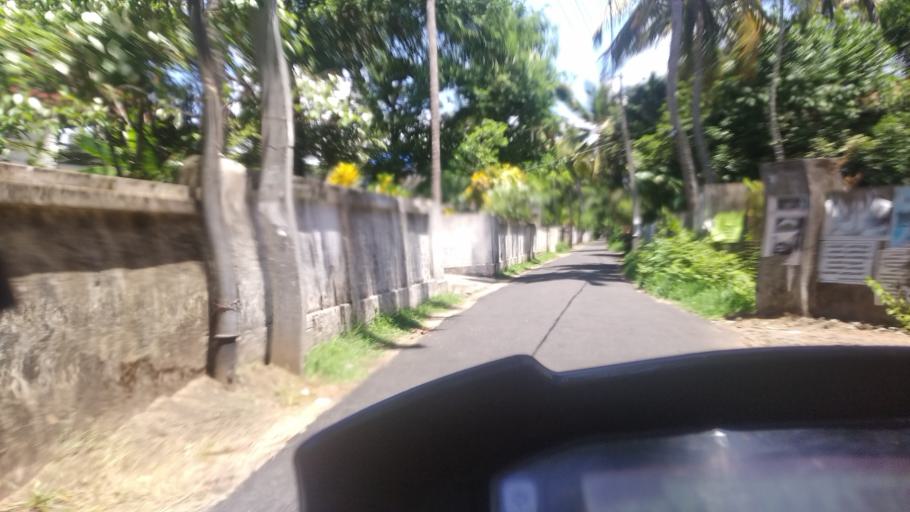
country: IN
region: Kerala
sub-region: Ernakulam
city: Elur
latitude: 10.0606
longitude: 76.2177
